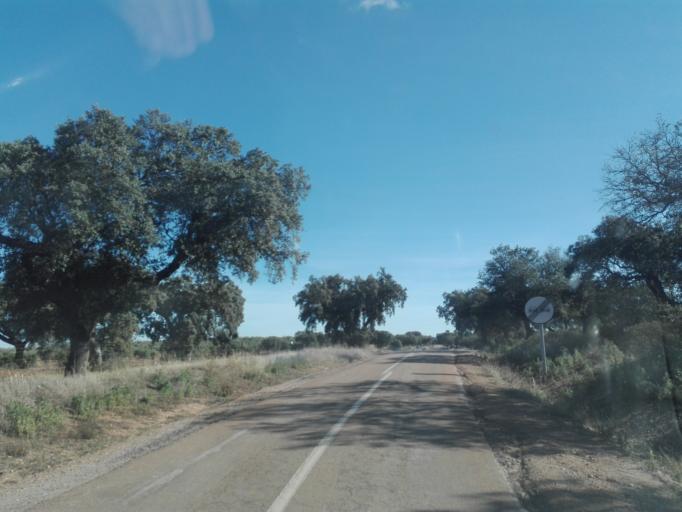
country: ES
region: Extremadura
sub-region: Provincia de Badajoz
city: Maguilla
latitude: 38.3375
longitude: -5.9293
